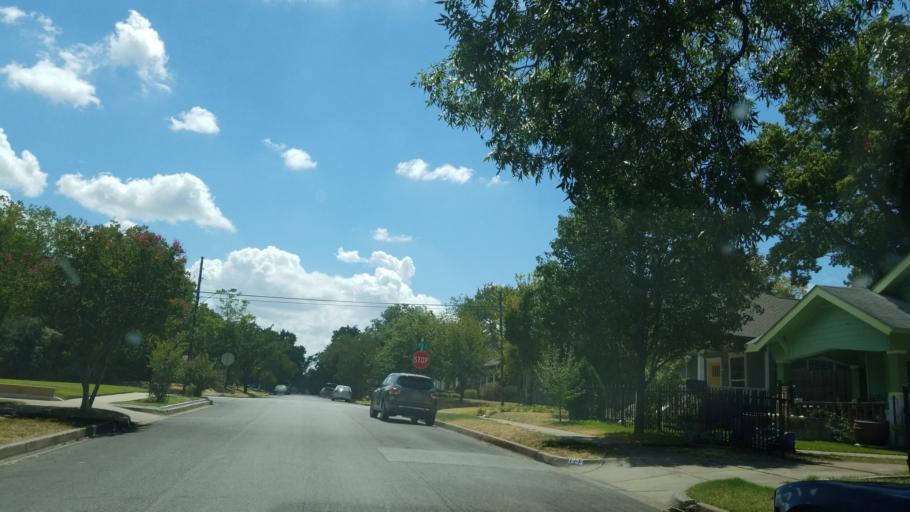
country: US
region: Texas
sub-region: Dallas County
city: Dallas
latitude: 32.7550
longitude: -96.8303
